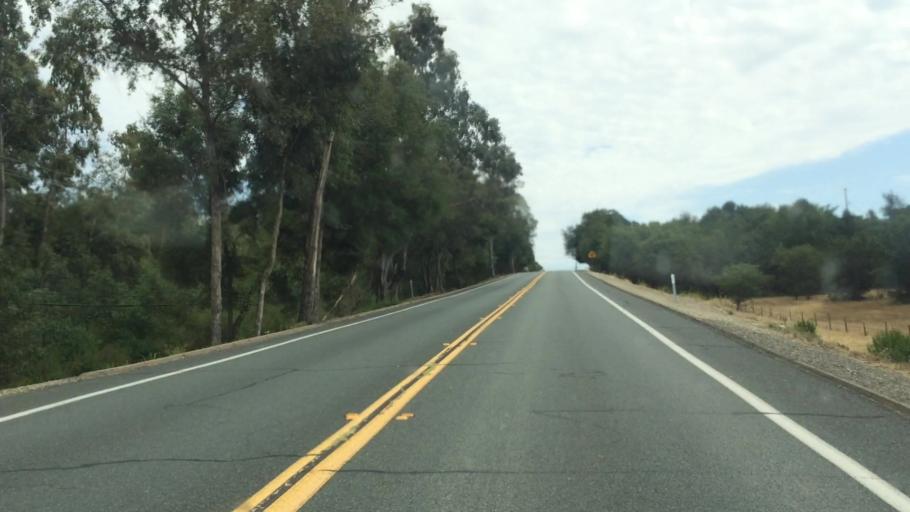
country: US
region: California
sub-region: Amador County
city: Ione
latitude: 38.3614
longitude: -120.9415
